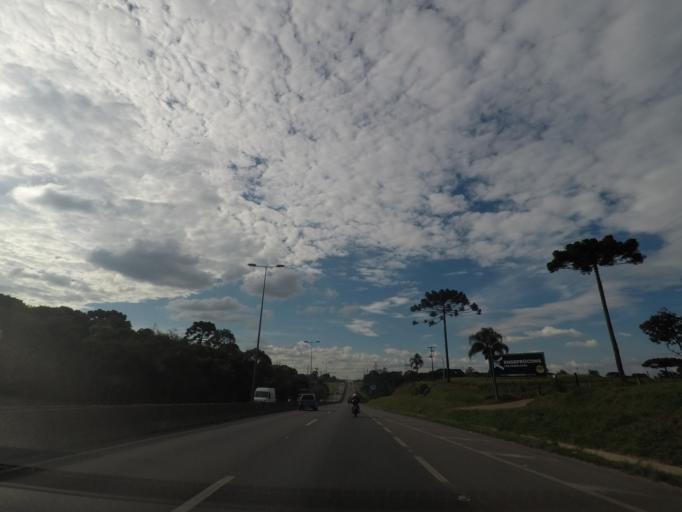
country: BR
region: Parana
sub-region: Araucaria
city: Araucaria
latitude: -25.6022
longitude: -49.3178
